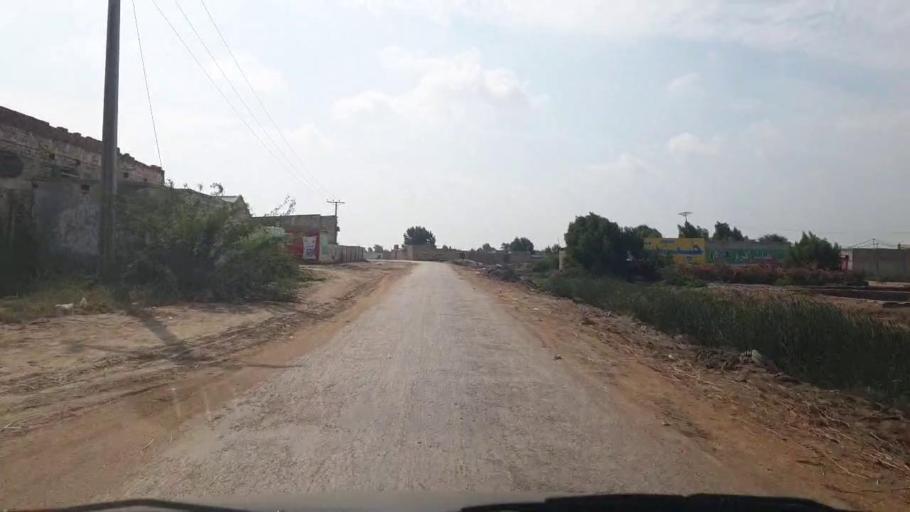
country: PK
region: Sindh
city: Kario
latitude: 24.6474
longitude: 68.5423
